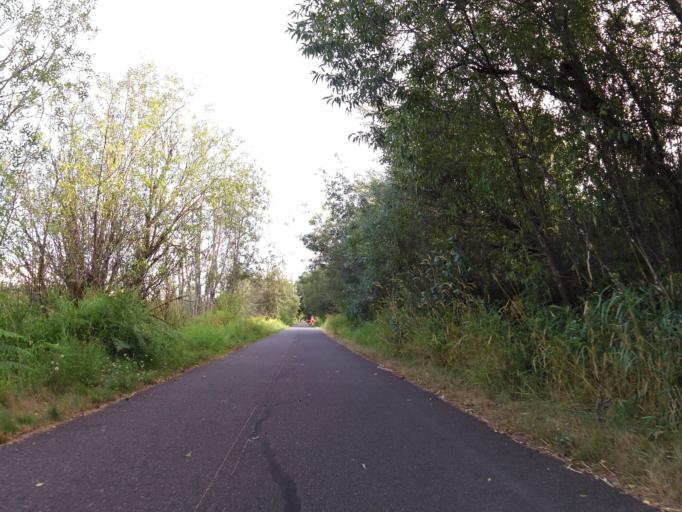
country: US
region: Washington
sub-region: Thurston County
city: Lacey
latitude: 47.0187
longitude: -122.8340
